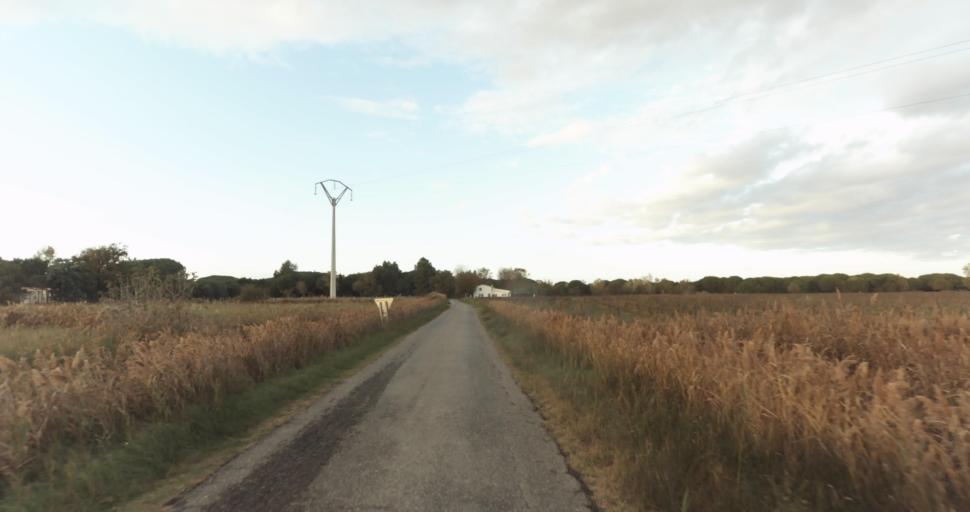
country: FR
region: Languedoc-Roussillon
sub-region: Departement du Gard
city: Aigues-Mortes
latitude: 43.5797
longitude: 4.1865
